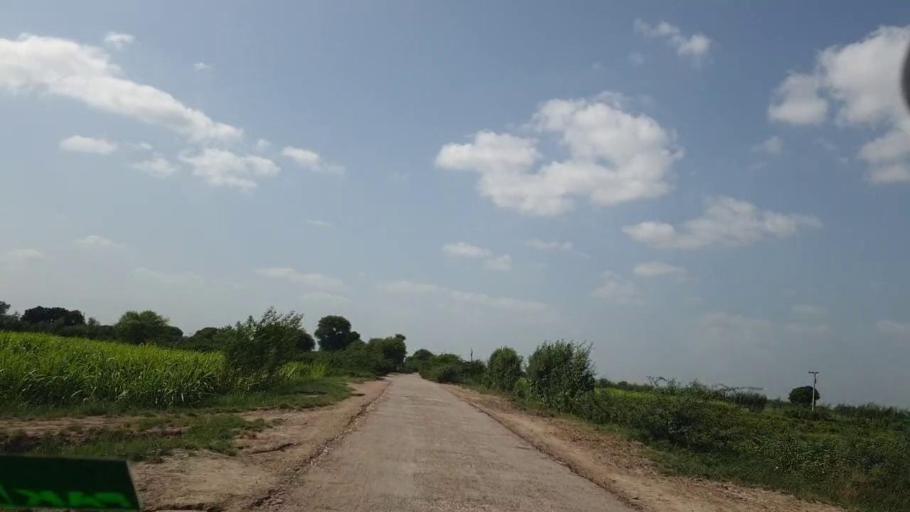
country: PK
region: Sindh
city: Naukot
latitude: 24.6524
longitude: 69.2165
